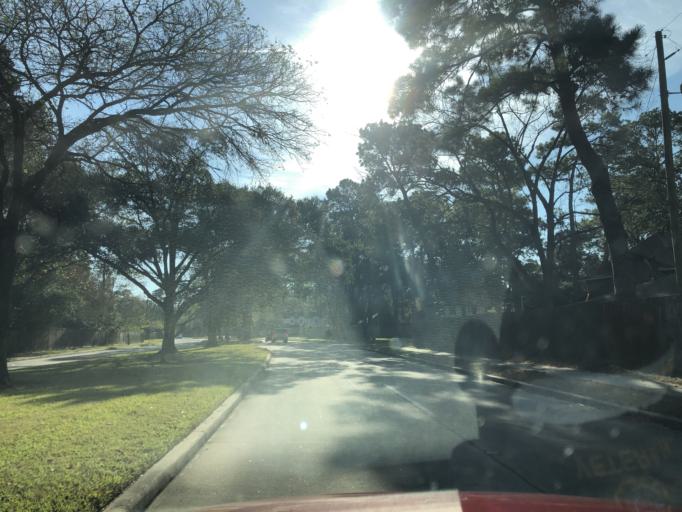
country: US
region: Texas
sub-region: Harris County
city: Tomball
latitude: 30.0180
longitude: -95.5445
